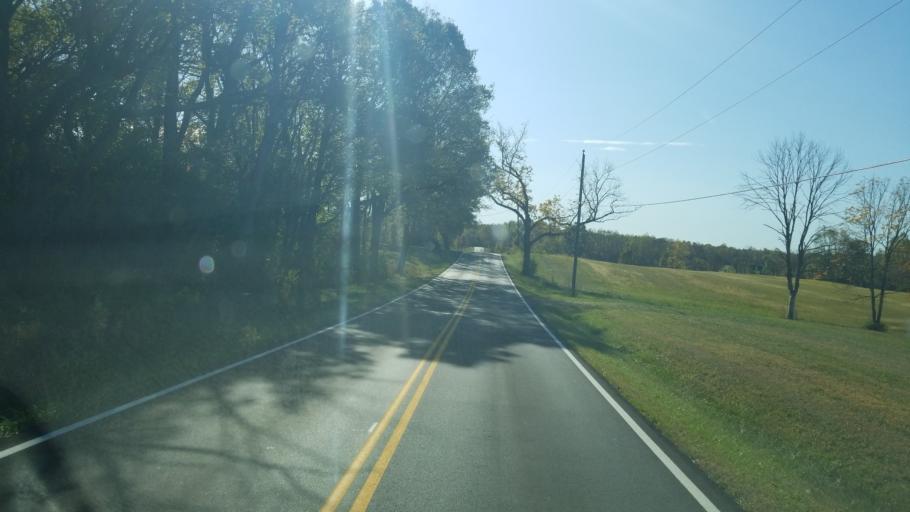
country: US
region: Ohio
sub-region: Warren County
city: Morrow
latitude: 39.3921
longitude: -84.0722
